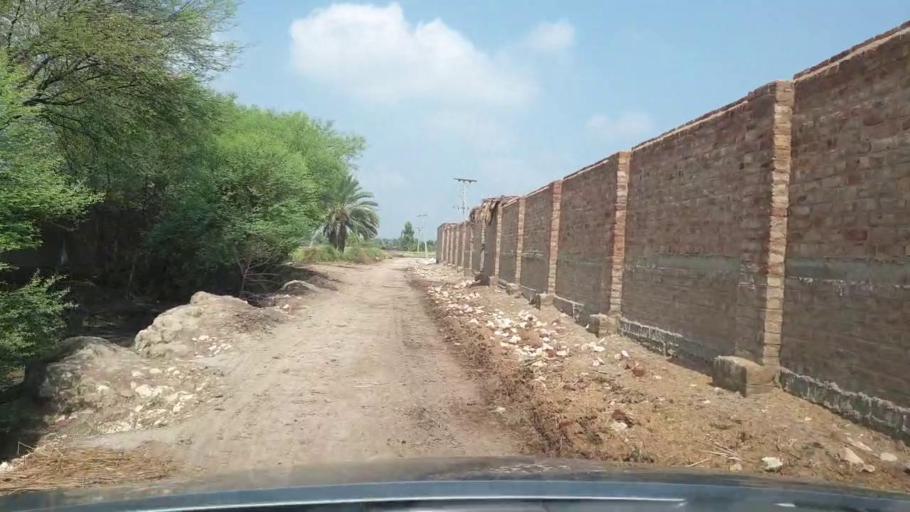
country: PK
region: Sindh
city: Pir jo Goth
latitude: 27.6049
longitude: 68.6980
